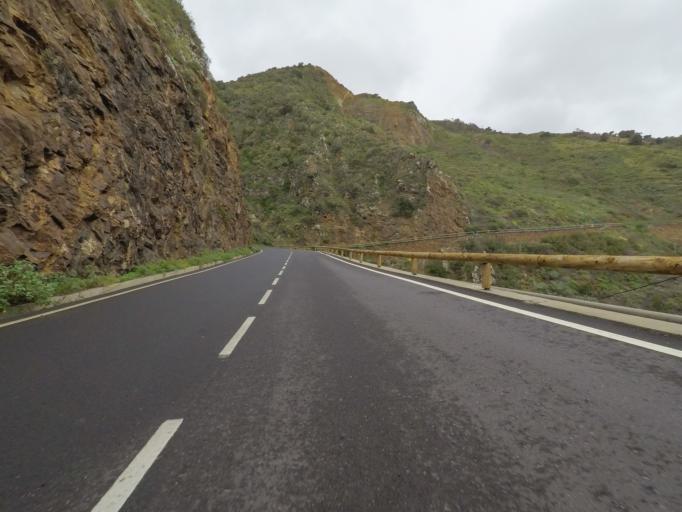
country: ES
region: Canary Islands
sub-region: Provincia de Santa Cruz de Tenerife
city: Agulo
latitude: 28.1872
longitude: -17.2118
